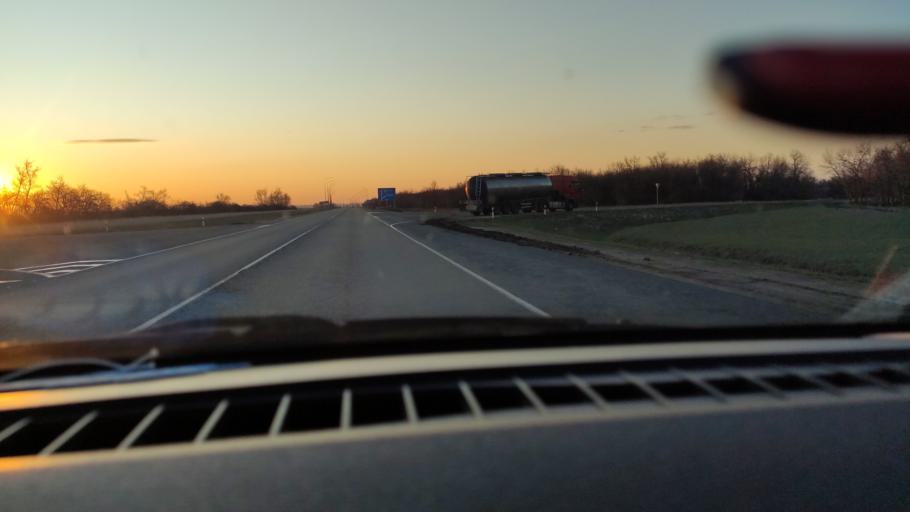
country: RU
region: Saratov
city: Yelshanka
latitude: 51.8203
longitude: 46.3476
